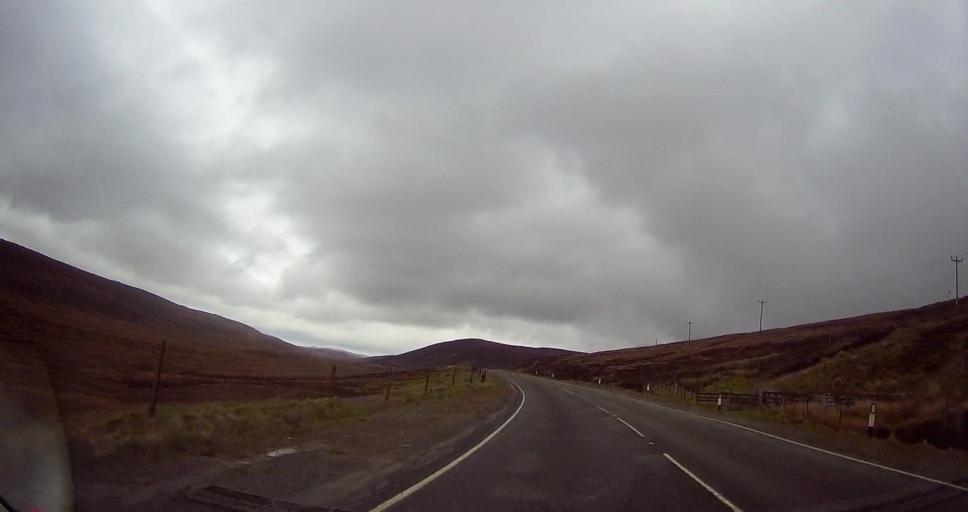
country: GB
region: Scotland
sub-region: Shetland Islands
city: Lerwick
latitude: 60.2936
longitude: -1.2396
